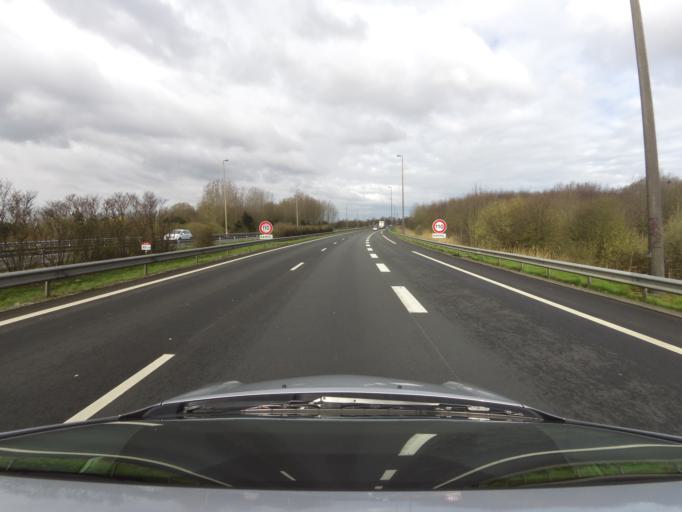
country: FR
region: Nord-Pas-de-Calais
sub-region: Departement du Pas-de-Calais
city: Coulogne
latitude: 50.9338
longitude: 1.8849
